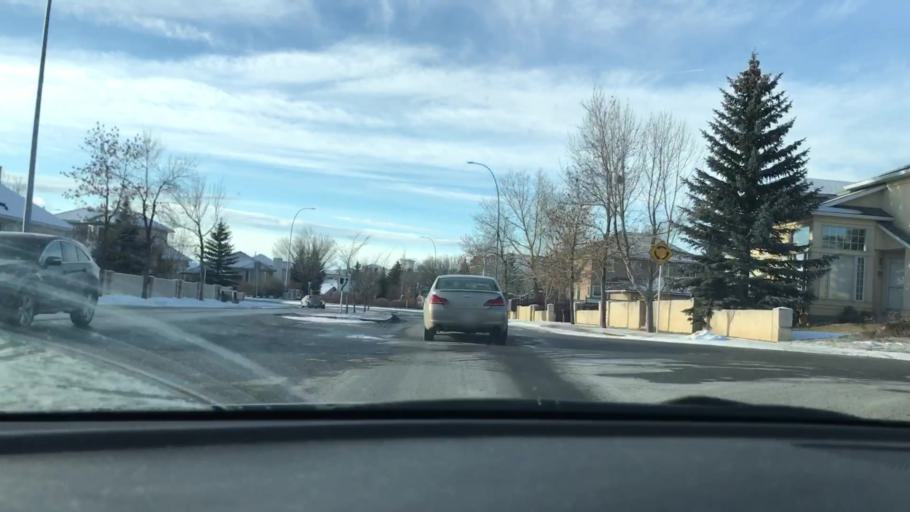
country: CA
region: Alberta
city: Calgary
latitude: 51.0205
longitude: -114.1821
